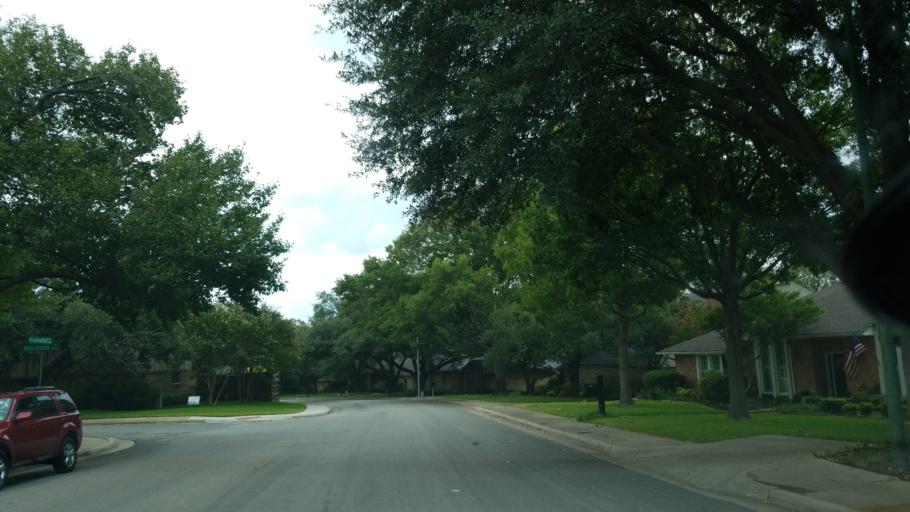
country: US
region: Texas
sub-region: Dallas County
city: Richardson
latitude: 32.9012
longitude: -96.7328
